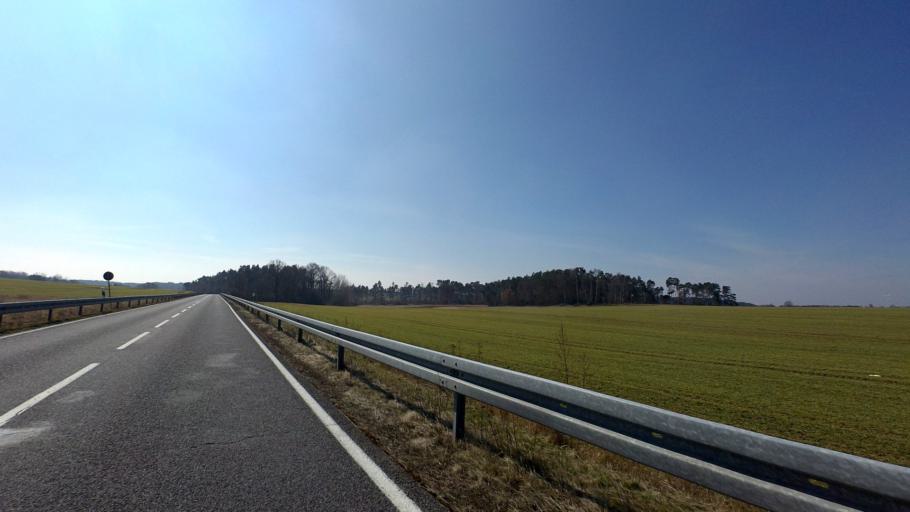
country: DE
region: Saxony-Anhalt
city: Nudersdorf
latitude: 51.9628
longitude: 12.5880
